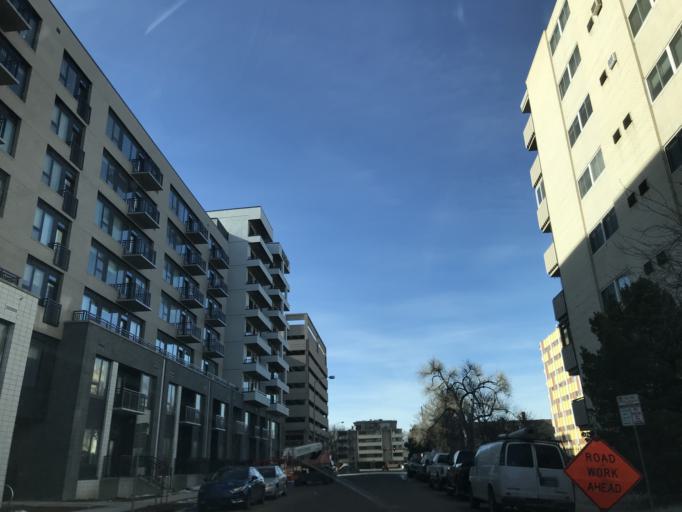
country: US
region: Colorado
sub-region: Arapahoe County
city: Glendale
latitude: 39.7329
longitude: -104.9384
